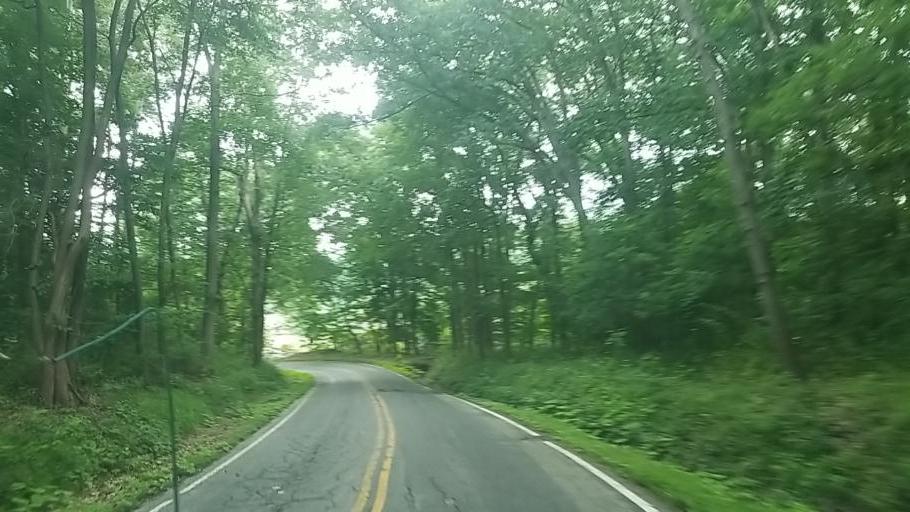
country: US
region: Ohio
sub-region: Muskingum County
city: Frazeysburg
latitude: 40.1631
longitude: -82.2584
